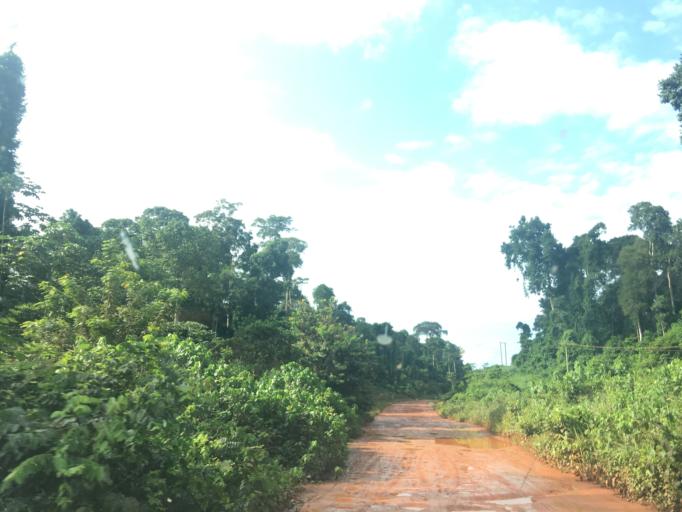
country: GH
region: Western
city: Wassa-Akropong
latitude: 5.9680
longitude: -2.4210
